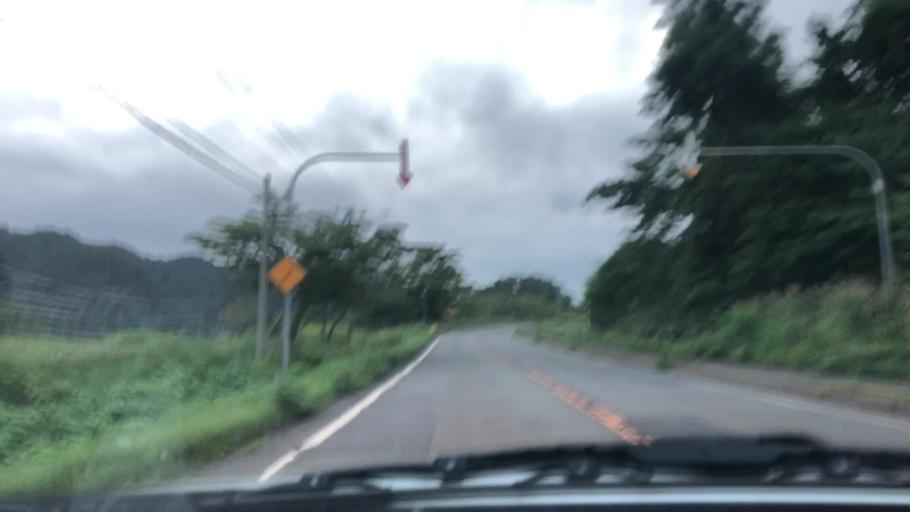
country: JP
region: Hokkaido
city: Chitose
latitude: 42.9066
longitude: 141.9913
